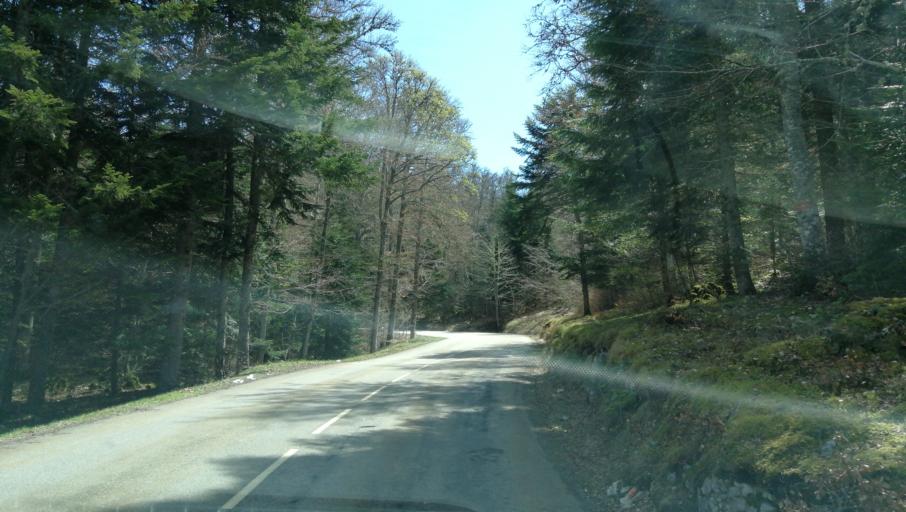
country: FR
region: Rhone-Alpes
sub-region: Departement de la Drome
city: Die
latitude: 44.8747
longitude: 5.4023
